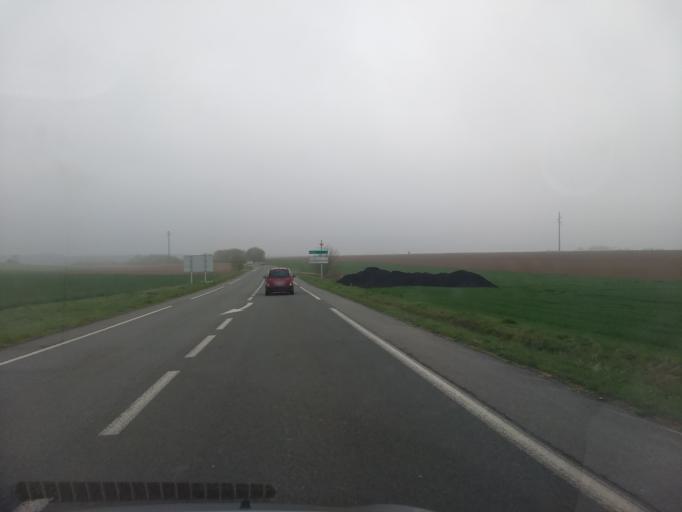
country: FR
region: Nord-Pas-de-Calais
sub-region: Departement du Pas-de-Calais
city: Montreuil
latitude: 50.4281
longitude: 1.7277
